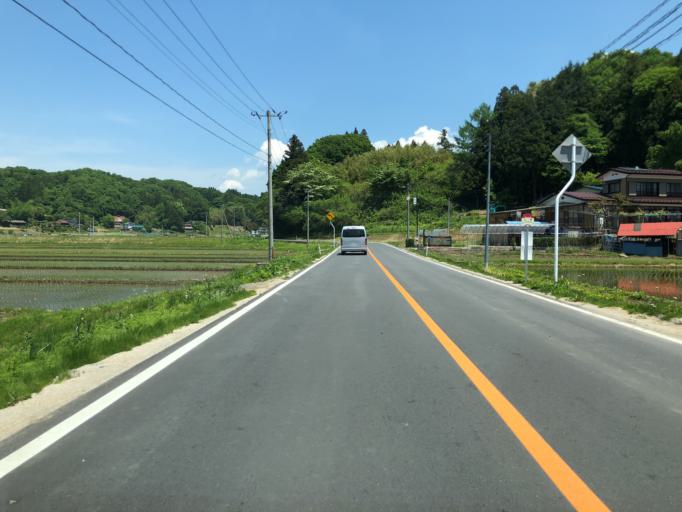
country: JP
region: Fukushima
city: Funehikimachi-funehiki
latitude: 37.4978
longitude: 140.5926
